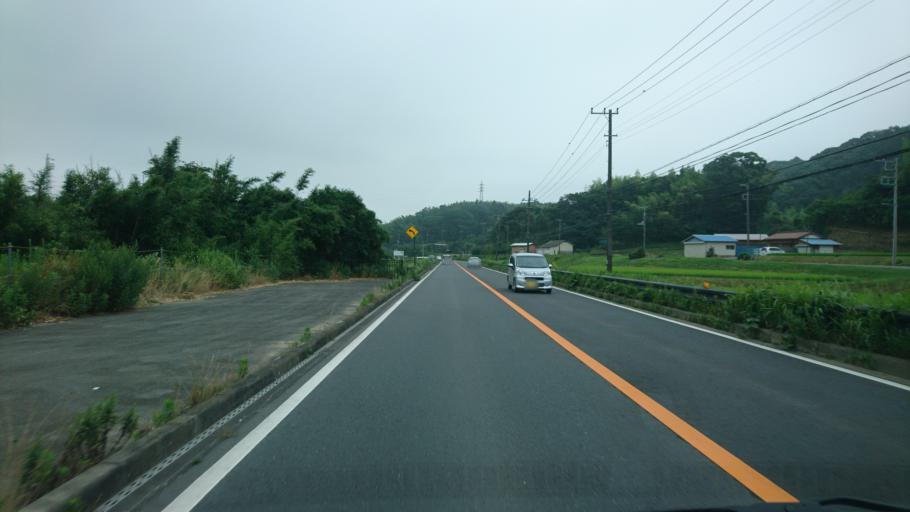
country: JP
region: Chiba
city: Kimitsu
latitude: 35.2716
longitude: 139.8984
